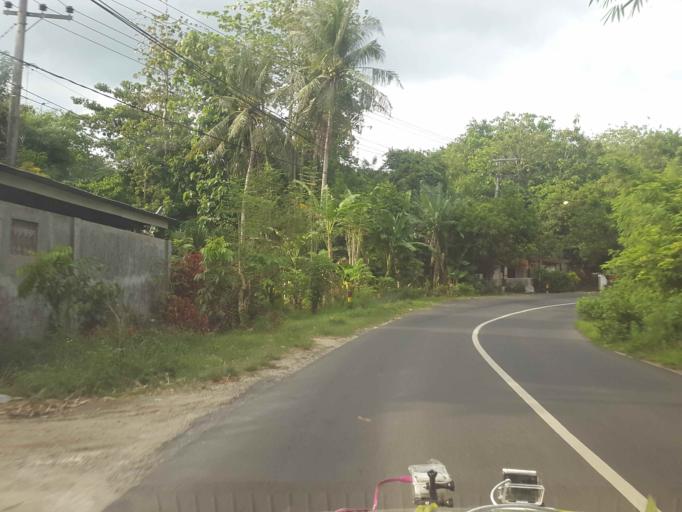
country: ID
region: East Java
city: Senmasen
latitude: -6.9891
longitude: 113.8631
